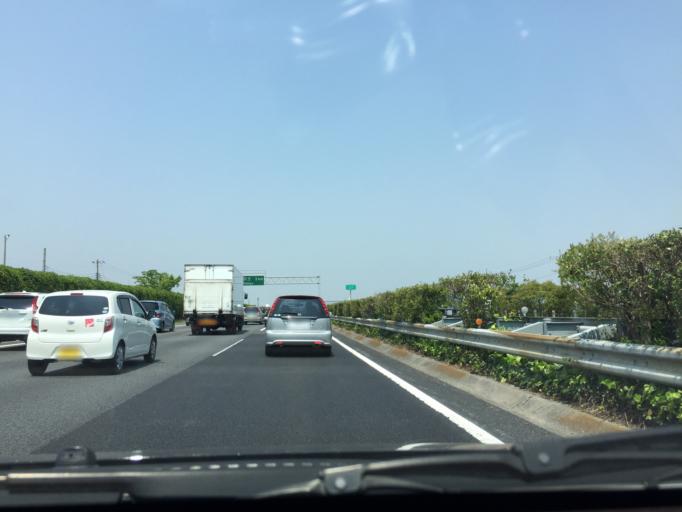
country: JP
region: Saitama
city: Kazo
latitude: 36.1498
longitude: 139.5992
